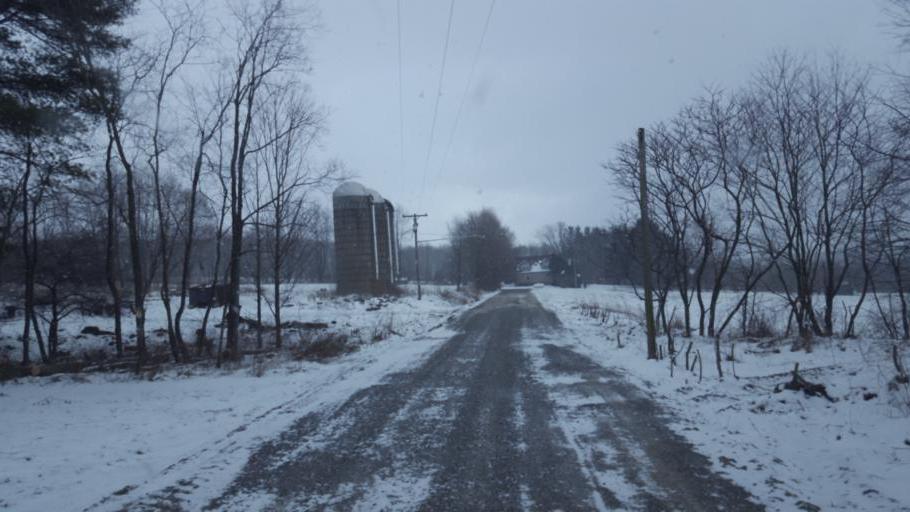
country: US
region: Pennsylvania
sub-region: Mercer County
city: Stoneboro
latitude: 41.4242
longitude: -80.0699
